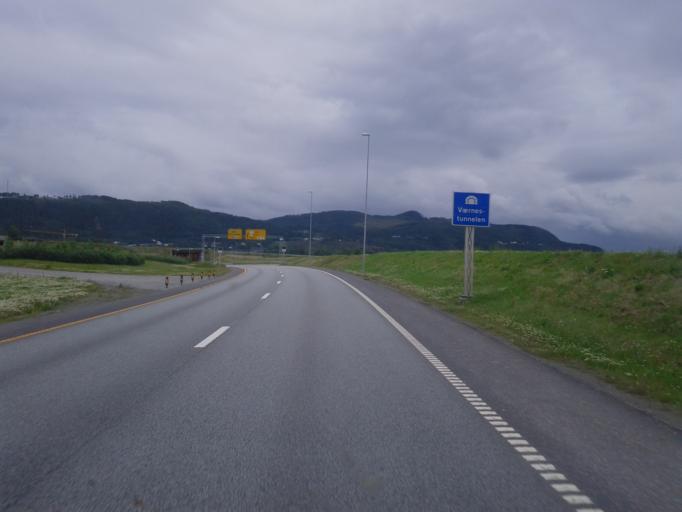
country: NO
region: Nord-Trondelag
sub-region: Stjordal
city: Stjordal
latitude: 63.4605
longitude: 10.9105
